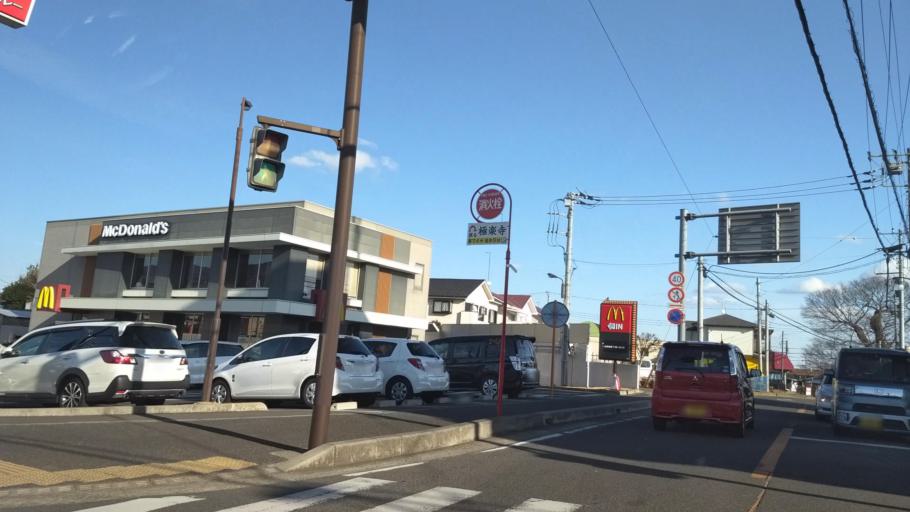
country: JP
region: Kanagawa
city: Isehara
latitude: 35.3783
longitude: 139.2775
